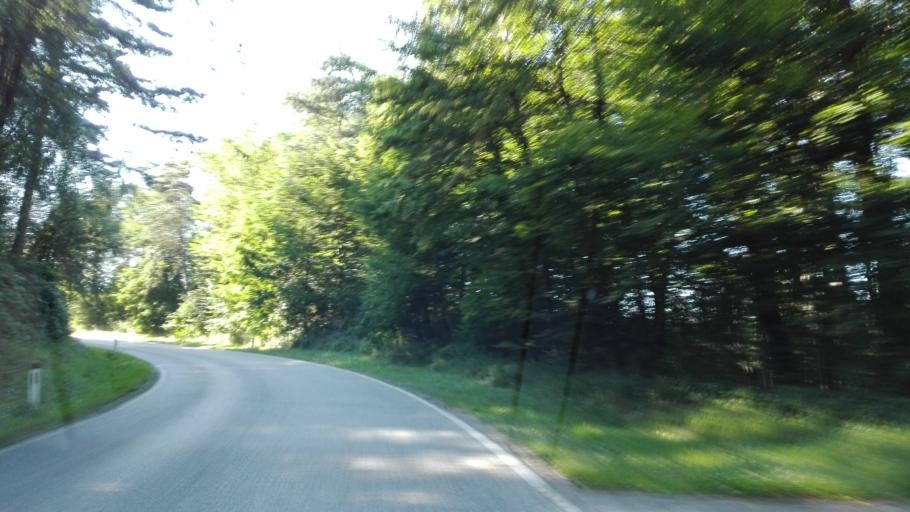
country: AT
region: Lower Austria
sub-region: Politischer Bezirk Sankt Polten
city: Eichgraben
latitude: 48.1540
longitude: 15.9728
